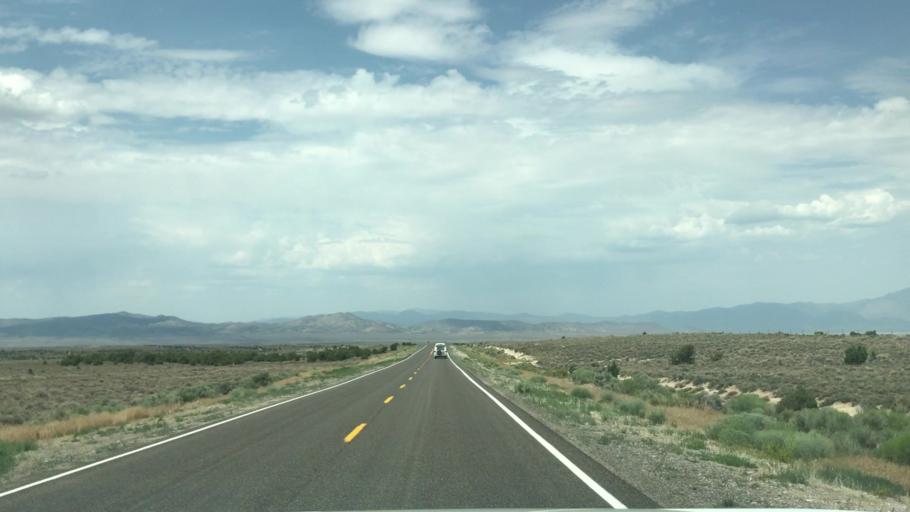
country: US
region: Nevada
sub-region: Eureka County
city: Eureka
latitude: 39.3927
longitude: -115.5140
